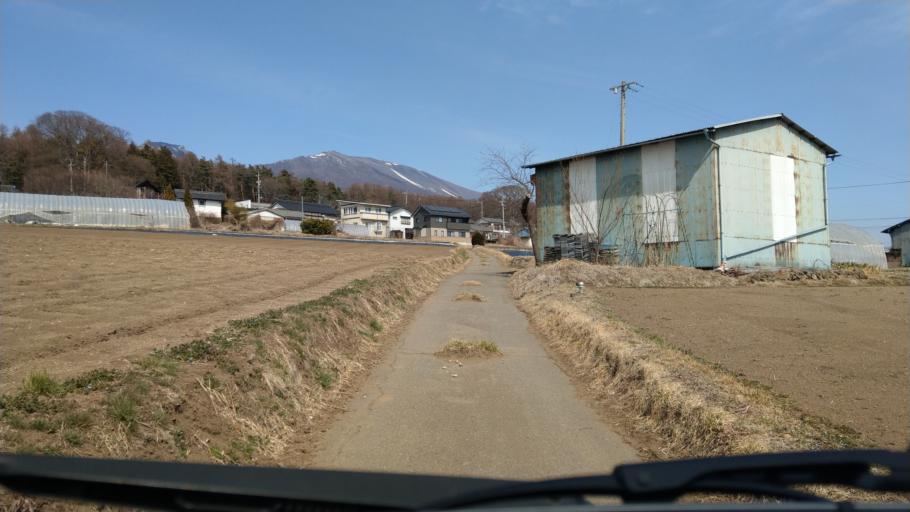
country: JP
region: Nagano
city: Komoro
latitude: 36.3327
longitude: 138.4620
